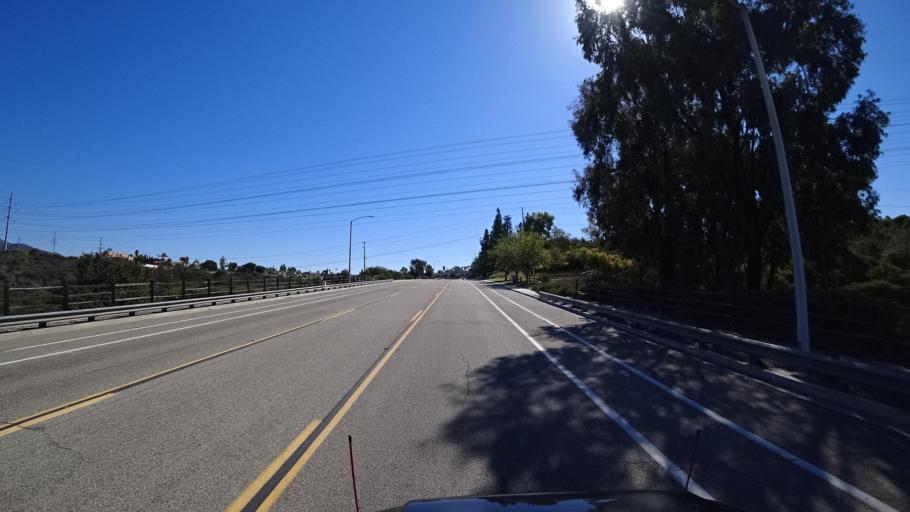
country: US
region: California
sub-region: San Diego County
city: Bonita
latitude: 32.6583
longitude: -116.9956
